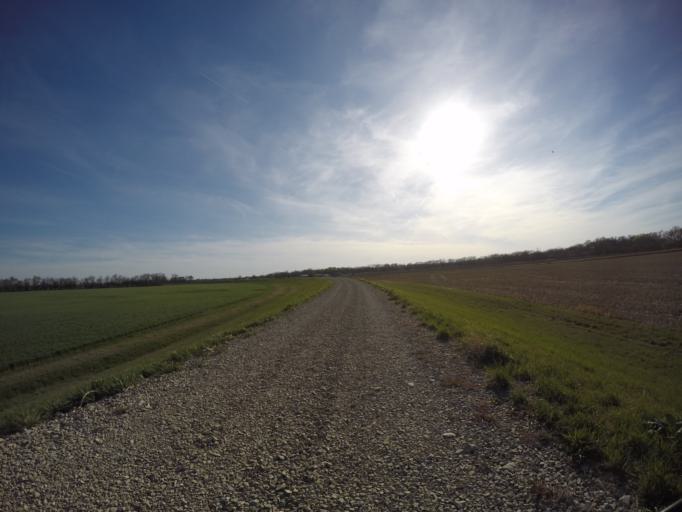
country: US
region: Kansas
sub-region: Saline County
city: Salina
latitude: 38.8596
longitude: -97.6282
